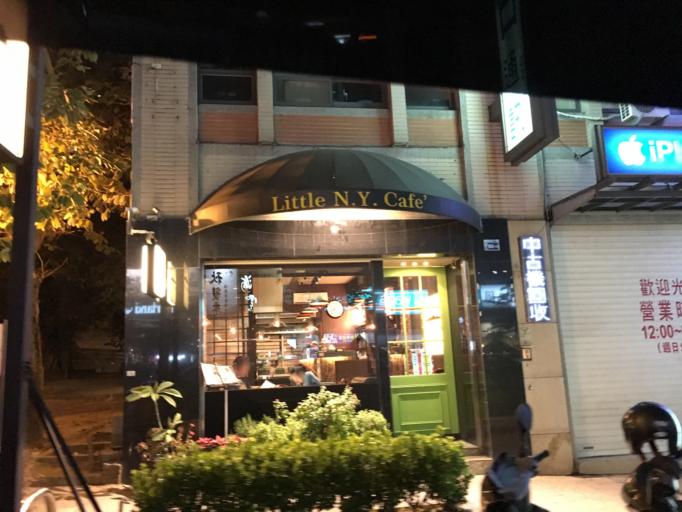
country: TW
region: Taiwan
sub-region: Taichung City
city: Taichung
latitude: 24.1906
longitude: 120.6120
